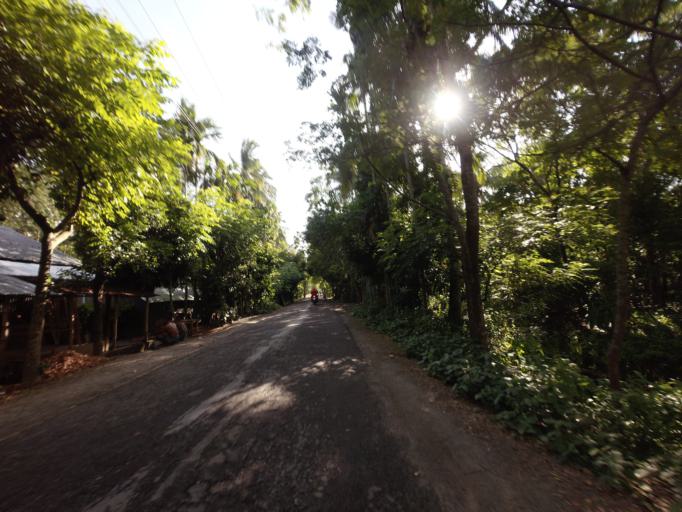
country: BD
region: Khulna
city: Kalia
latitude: 23.0135
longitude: 89.5919
